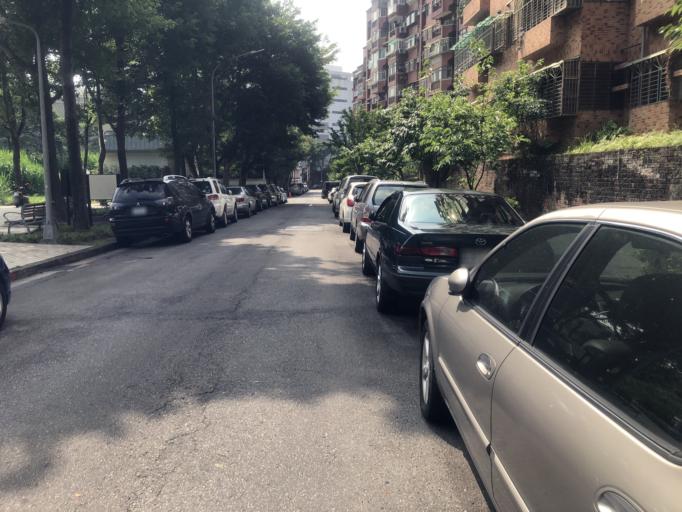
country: TW
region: Taipei
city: Taipei
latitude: 25.0841
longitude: 121.5385
